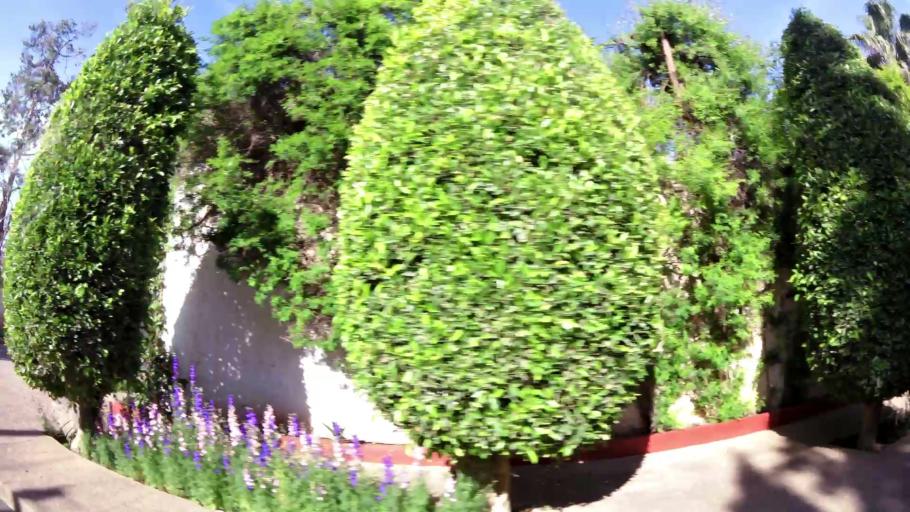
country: MA
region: Oriental
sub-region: Oujda-Angad
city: Oujda
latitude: 34.6653
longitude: -1.9028
